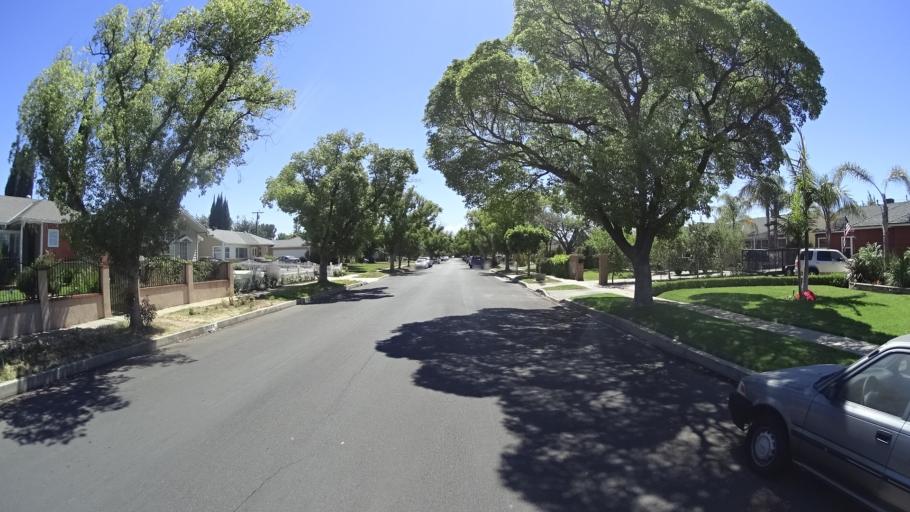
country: US
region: California
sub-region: Los Angeles County
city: San Fernando
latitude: 34.2509
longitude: -118.4576
